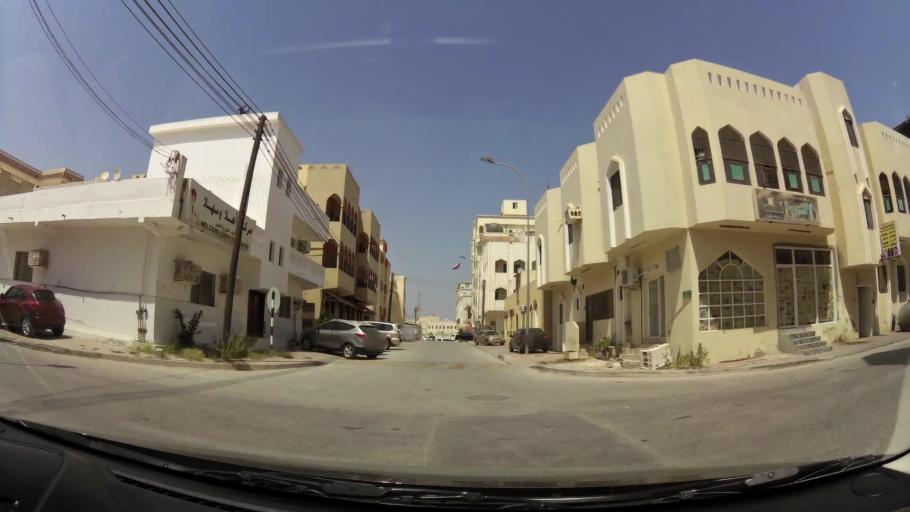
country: OM
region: Zufar
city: Salalah
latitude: 17.0182
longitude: 54.0870
